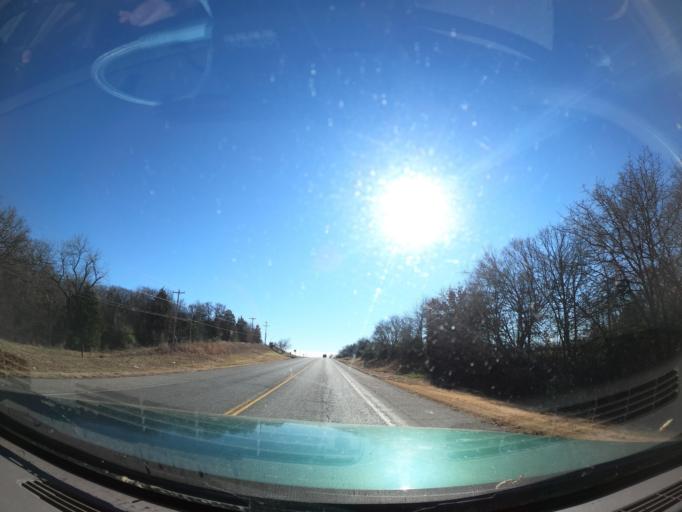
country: US
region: Oklahoma
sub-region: Muskogee County
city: Haskell
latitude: 35.8414
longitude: -95.6776
